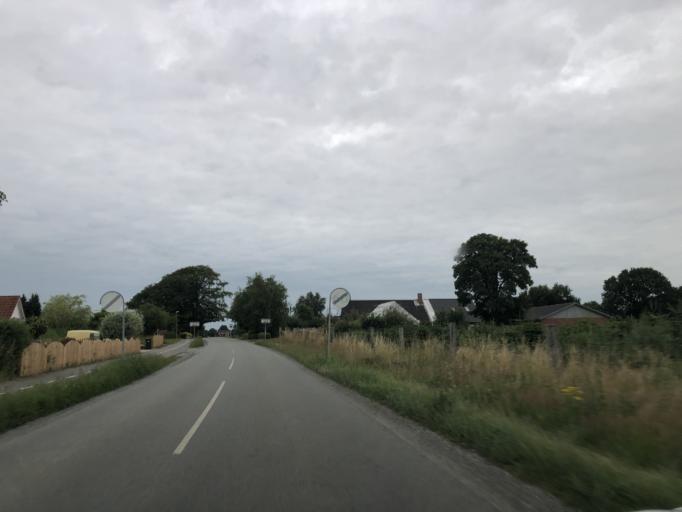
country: DK
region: South Denmark
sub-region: Vejle Kommune
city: Jelling
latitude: 55.7430
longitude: 9.4141
